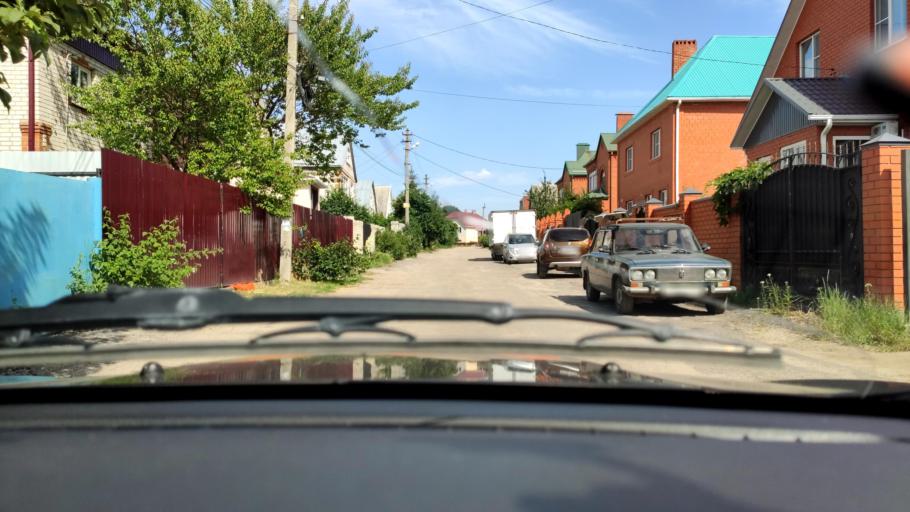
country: RU
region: Voronezj
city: Podgornoye
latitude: 51.7434
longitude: 39.1558
